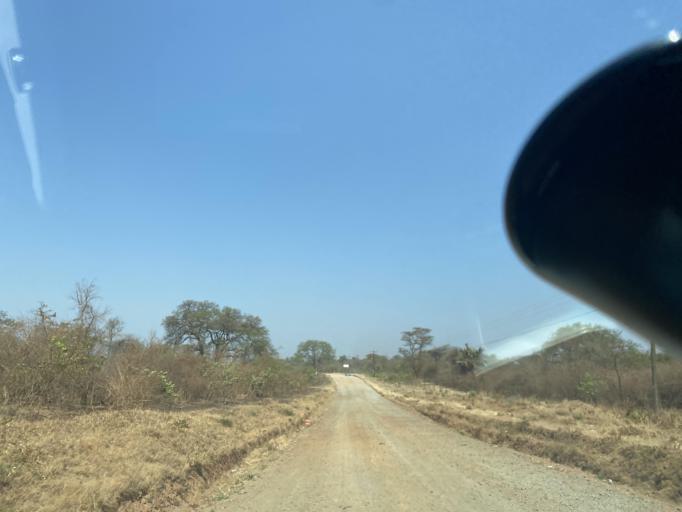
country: ZM
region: Lusaka
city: Lusaka
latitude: -15.5245
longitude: 28.1062
